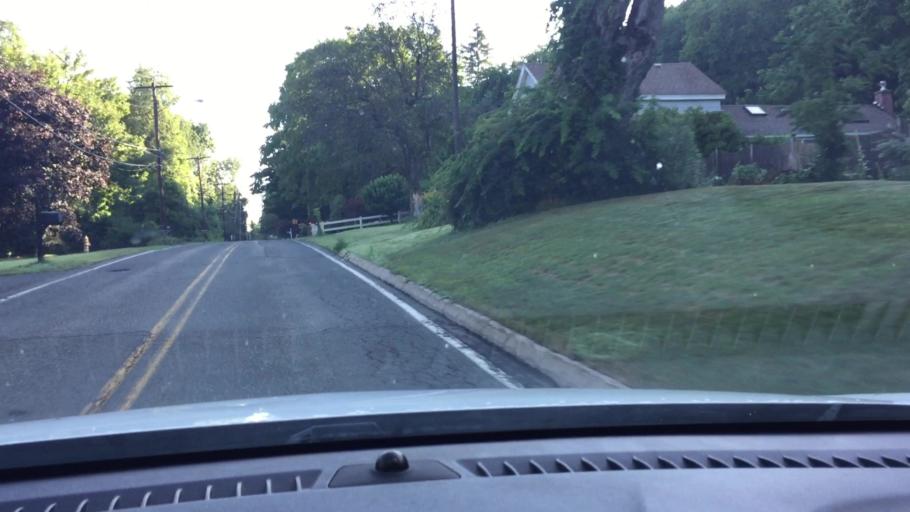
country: US
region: Massachusetts
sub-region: Berkshire County
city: Pittsfield
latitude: 42.4098
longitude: -73.2323
